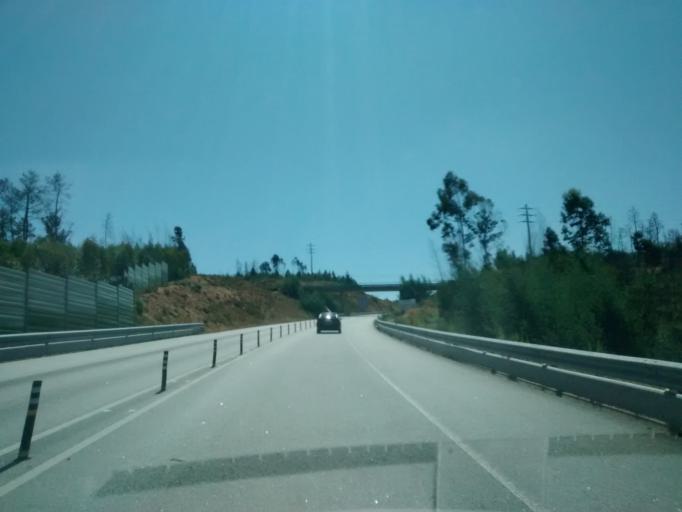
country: PT
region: Coimbra
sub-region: Tabua
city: Tabua
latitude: 40.3383
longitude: -7.9725
